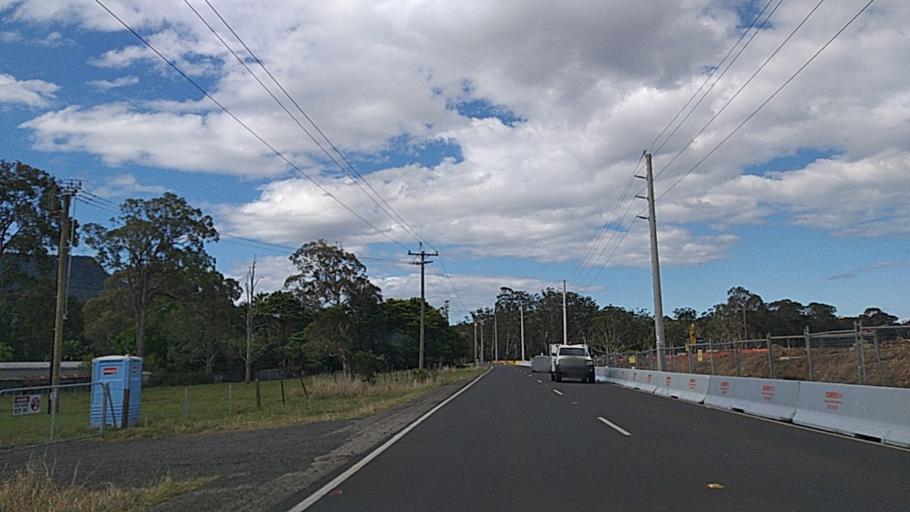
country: AU
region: New South Wales
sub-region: Wollongong
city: Dapto
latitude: -34.4764
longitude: 150.7872
